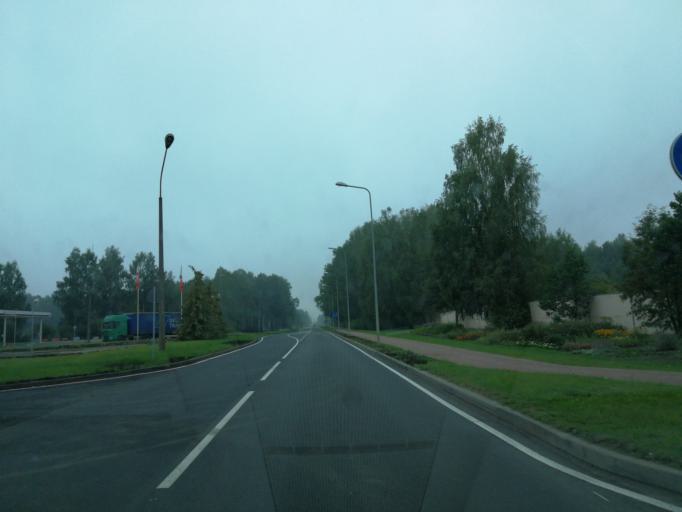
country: LV
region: Preilu Rajons
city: Preili
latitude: 56.2988
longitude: 26.7073
